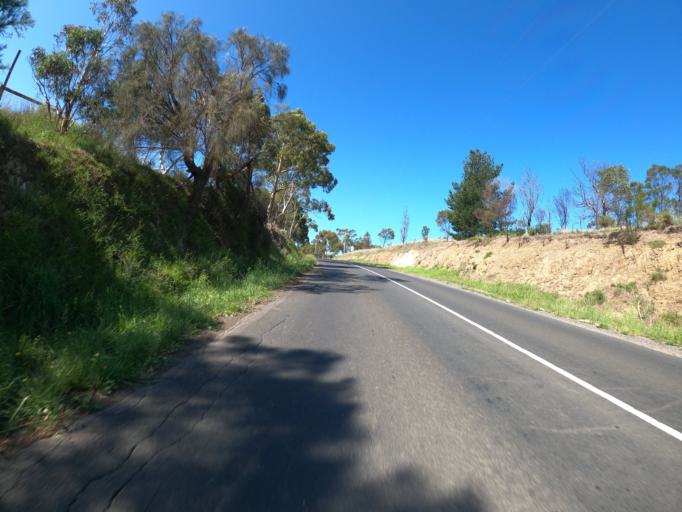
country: AU
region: Victoria
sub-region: Hume
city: Greenvale
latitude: -37.5510
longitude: 144.8664
